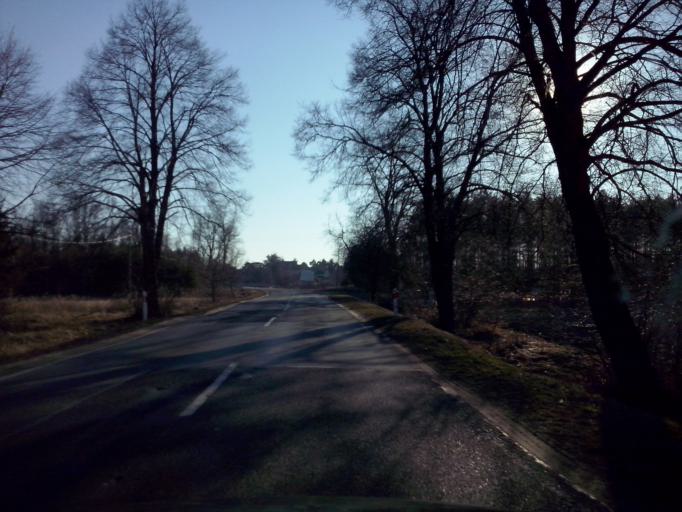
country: PL
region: Subcarpathian Voivodeship
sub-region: Powiat nizanski
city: Harasiuki
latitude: 50.4801
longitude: 22.4753
